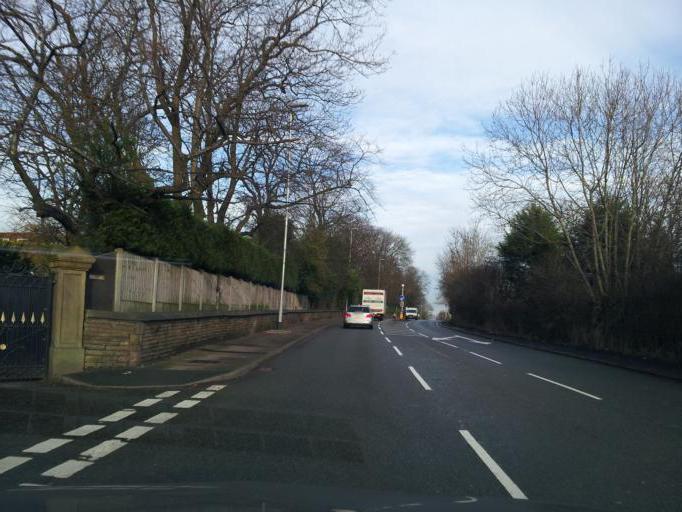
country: GB
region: England
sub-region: Manchester
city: Heywood
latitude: 53.5795
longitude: -2.2147
